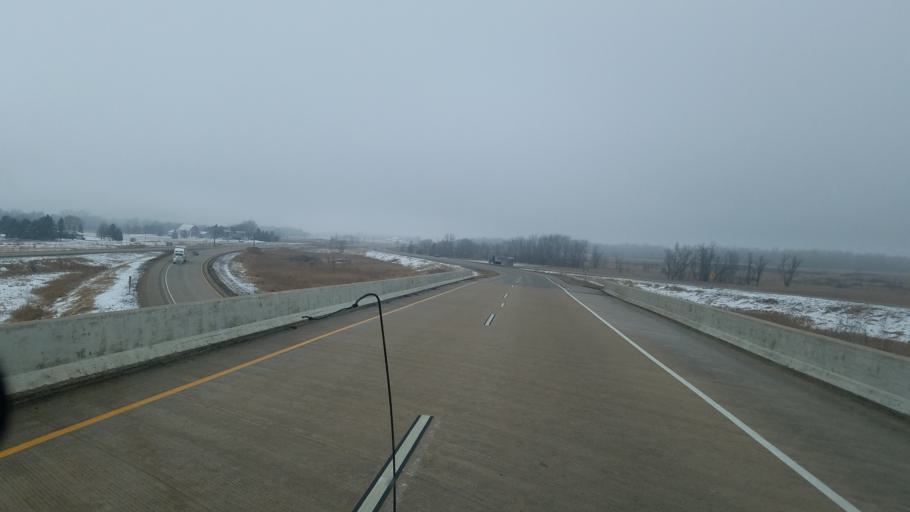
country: US
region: Wisconsin
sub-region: Winnebago County
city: Winneconne
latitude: 44.2086
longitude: -88.6847
